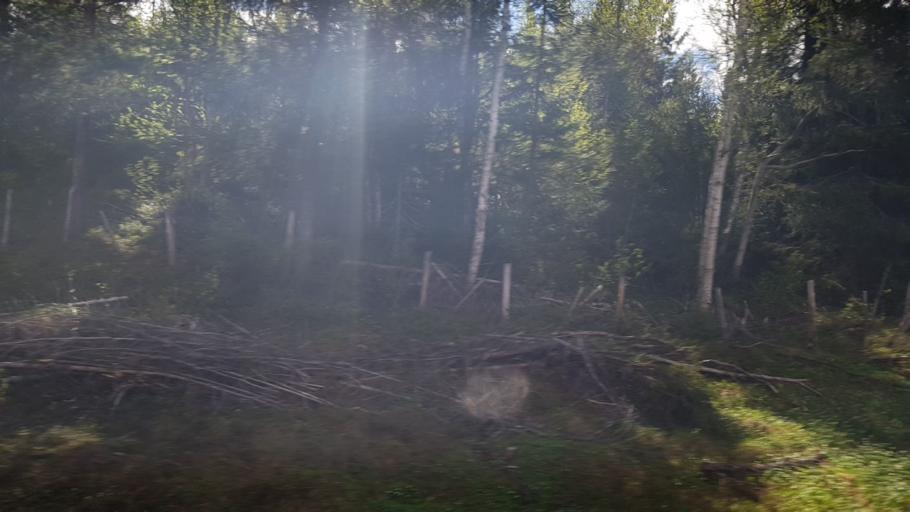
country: NO
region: Sor-Trondelag
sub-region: Rennebu
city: Berkak
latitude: 62.8998
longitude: 10.1118
